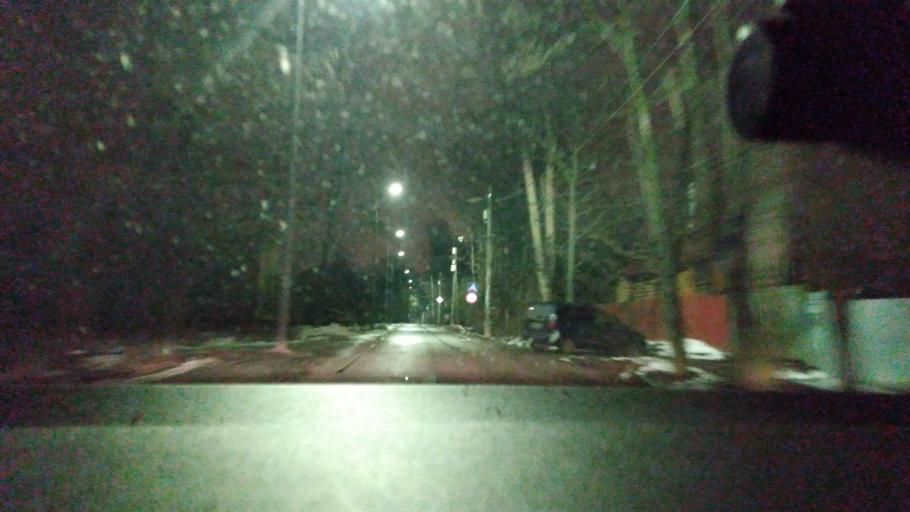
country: RU
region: Moskovskaya
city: Saltykovka
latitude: 55.7592
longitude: 37.9254
